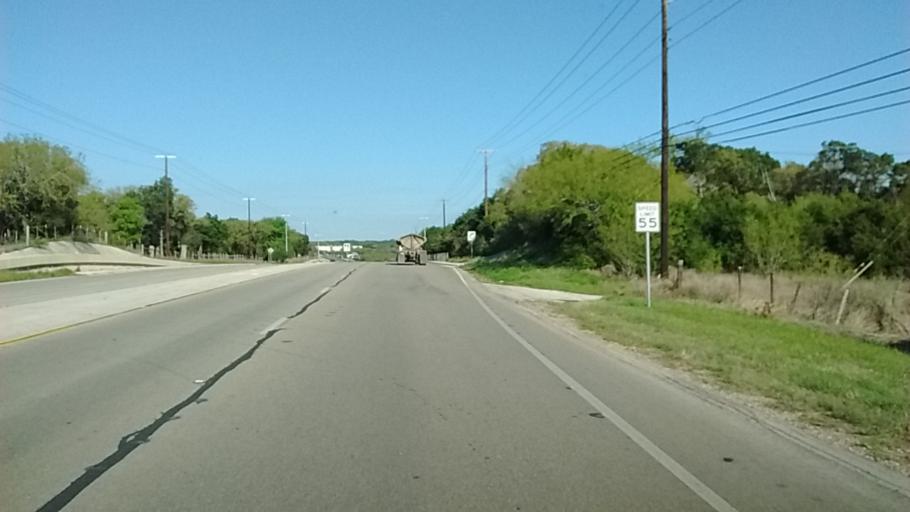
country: US
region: Texas
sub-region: Comal County
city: New Braunfels
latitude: 29.7336
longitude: -98.1963
